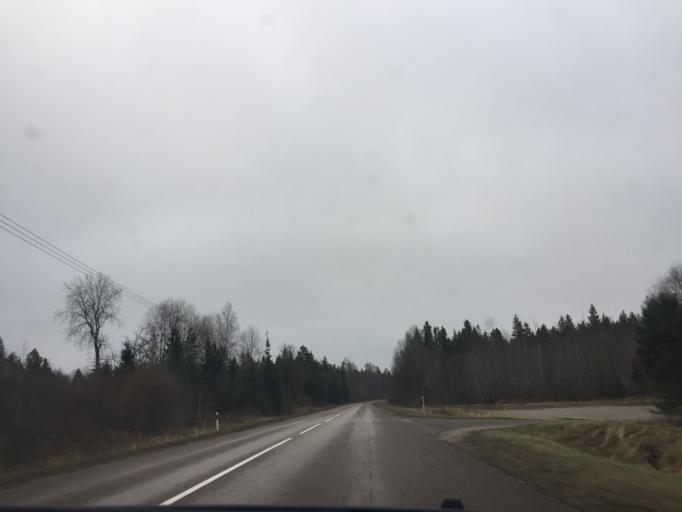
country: LV
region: Burtnieki
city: Matisi
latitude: 57.5152
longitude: 25.1525
